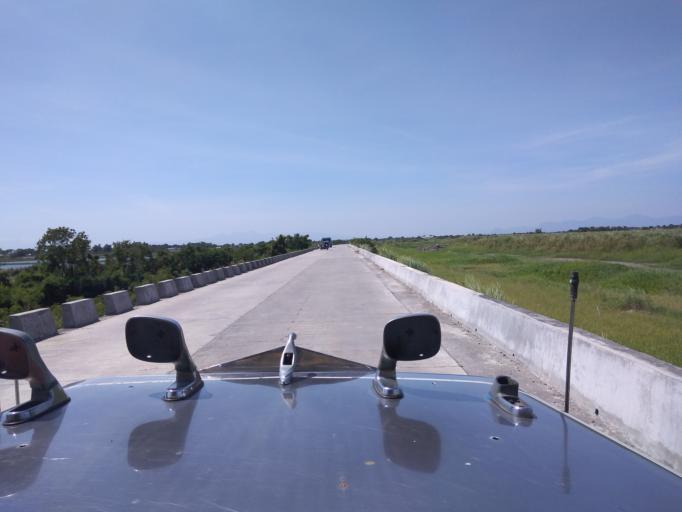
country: PH
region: Central Luzon
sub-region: Province of Pampanga
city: Minalin
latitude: 14.9684
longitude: 120.6756
